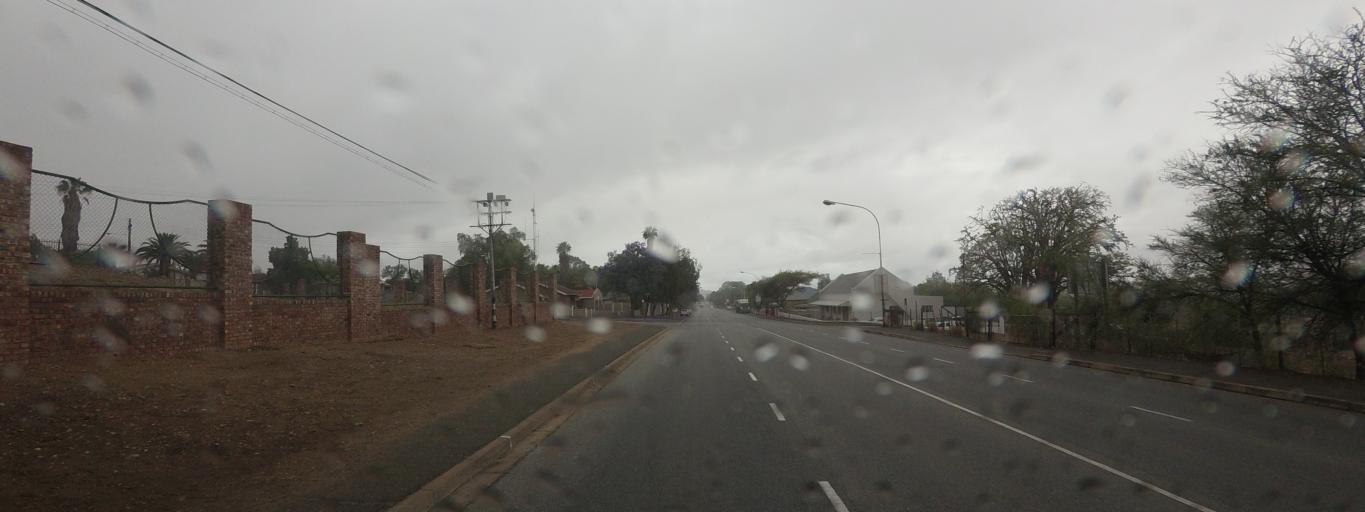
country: ZA
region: Western Cape
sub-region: Eden District Municipality
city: Oudtshoorn
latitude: -33.5774
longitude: 22.2056
